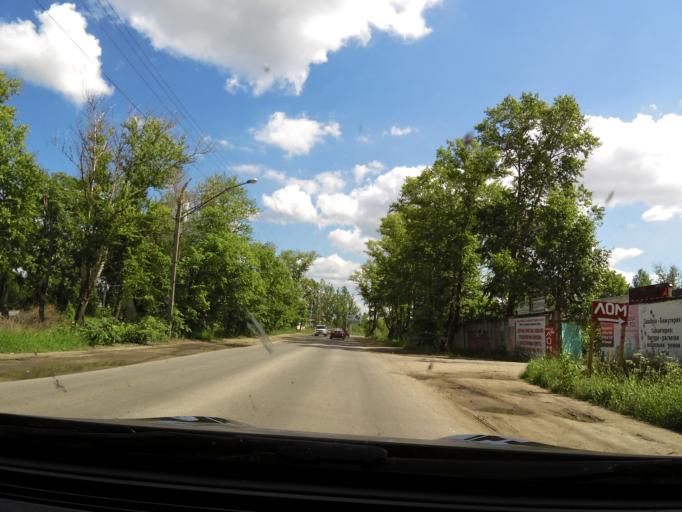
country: RU
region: Vologda
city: Vologda
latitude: 59.2346
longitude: 39.8309
